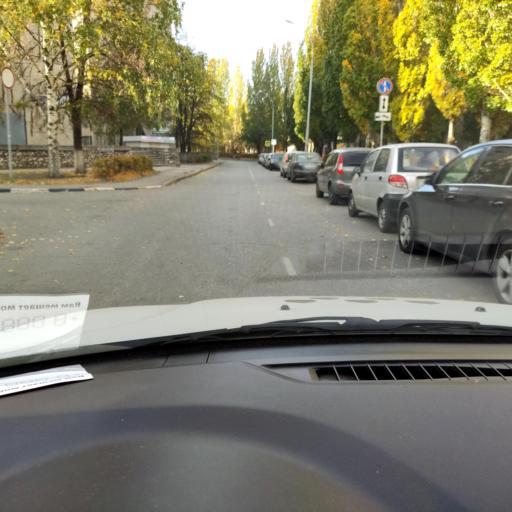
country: RU
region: Samara
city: Tol'yatti
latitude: 53.5318
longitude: 49.3058
